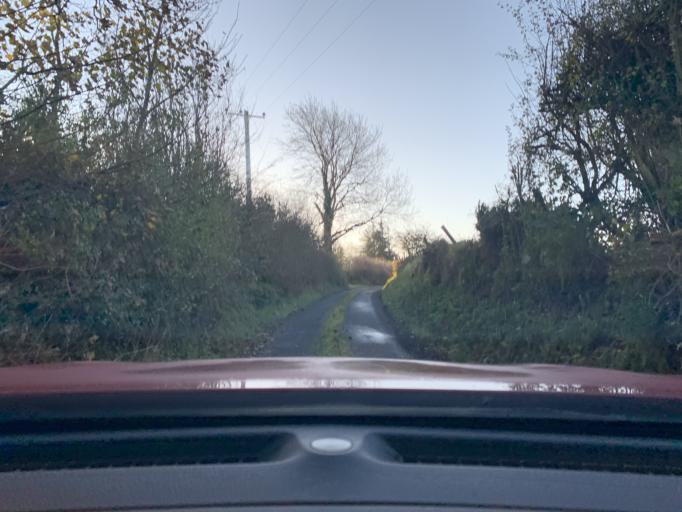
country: IE
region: Connaught
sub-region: Sligo
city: Ballymote
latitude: 54.0660
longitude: -8.5348
